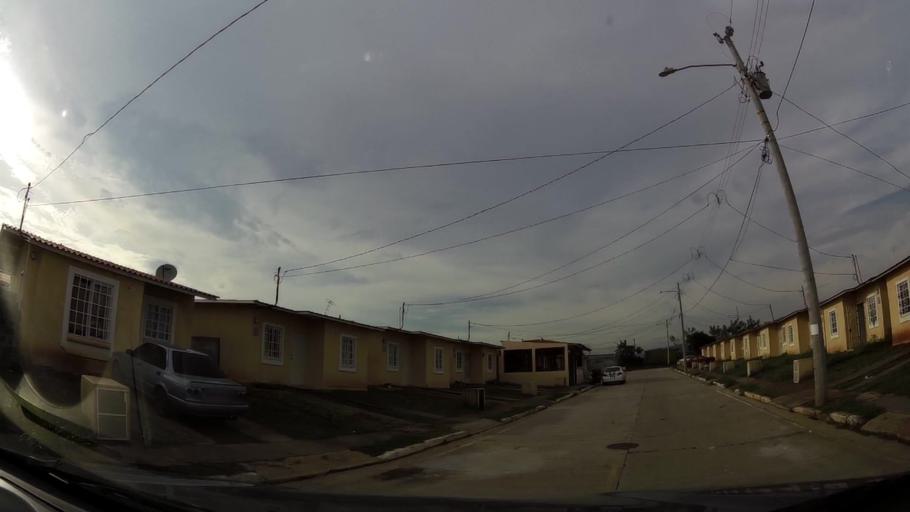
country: PA
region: Panama
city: Tocumen
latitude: 9.0766
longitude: -79.3551
